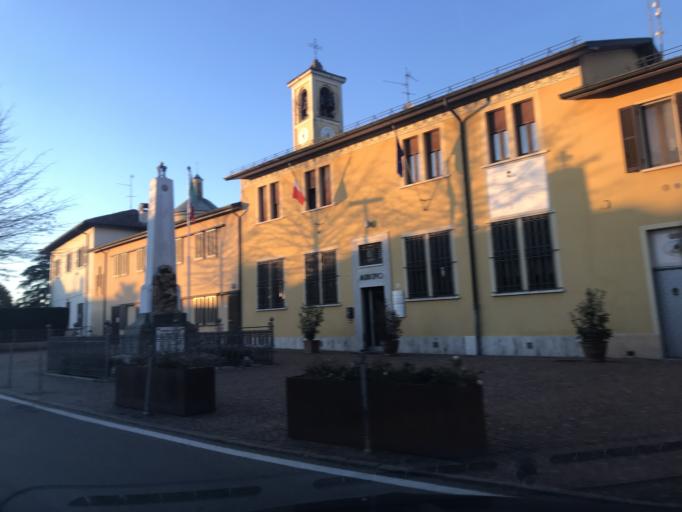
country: IT
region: Lombardy
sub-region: Provincia di Lodi
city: Pieve Fissiraga
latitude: 45.2638
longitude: 9.4592
